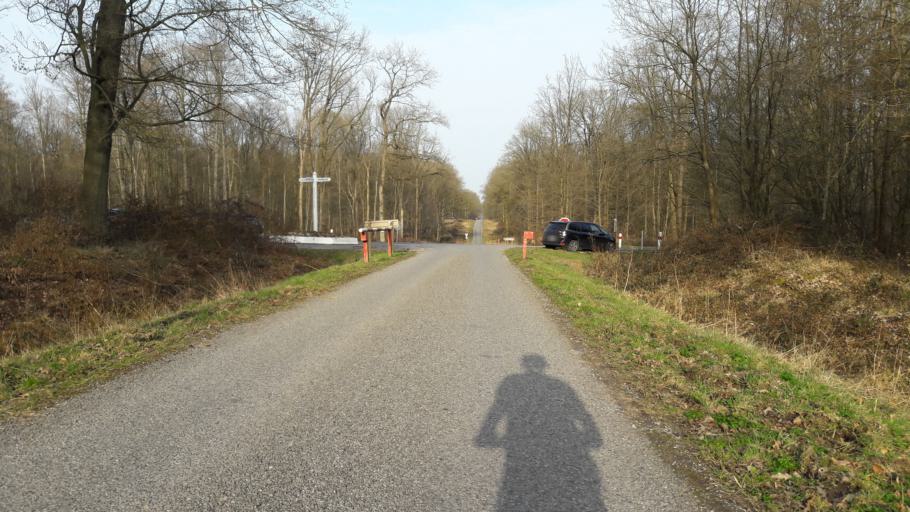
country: FR
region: Nord-Pas-de-Calais
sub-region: Departement du Nord
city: Maroilles
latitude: 50.1706
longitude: 3.7357
